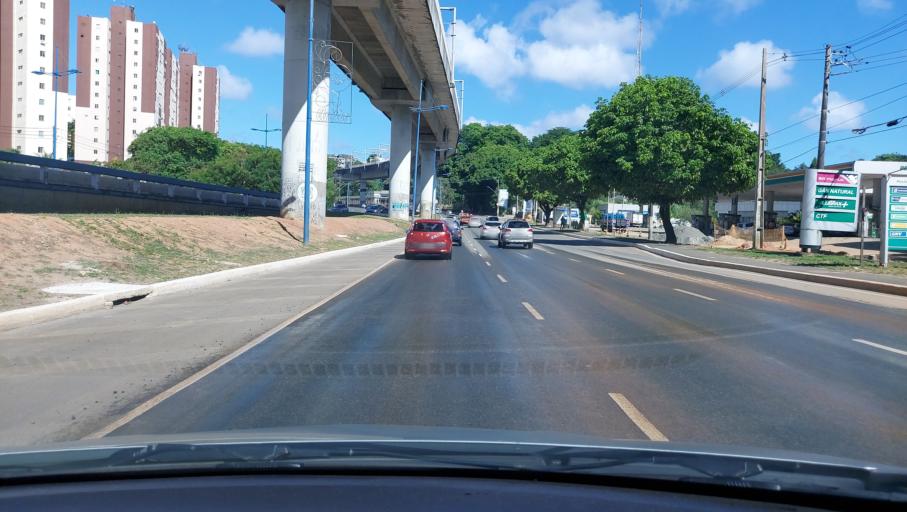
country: BR
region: Bahia
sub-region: Salvador
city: Salvador
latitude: -12.9816
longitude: -38.4954
